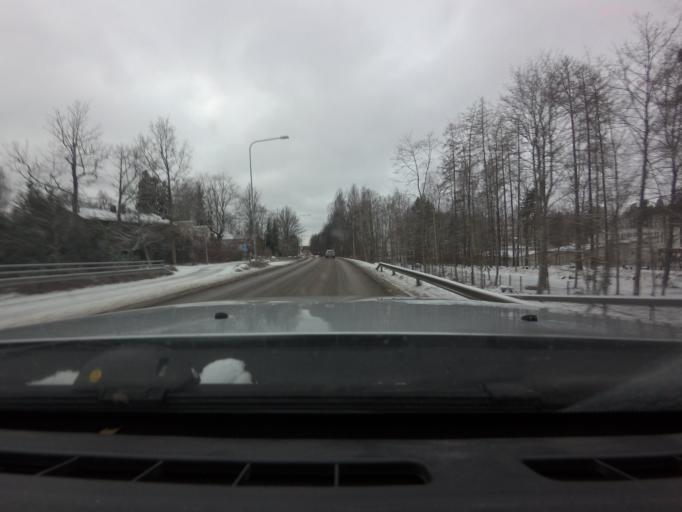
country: FI
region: Uusimaa
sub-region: Helsinki
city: Kauniainen
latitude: 60.2429
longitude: 24.7463
